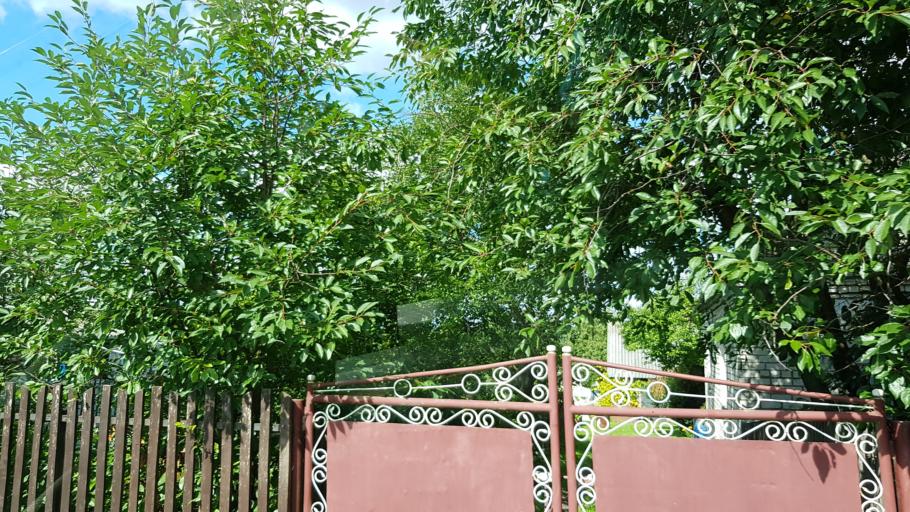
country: BY
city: Fanipol
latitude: 53.7607
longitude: 27.3278
